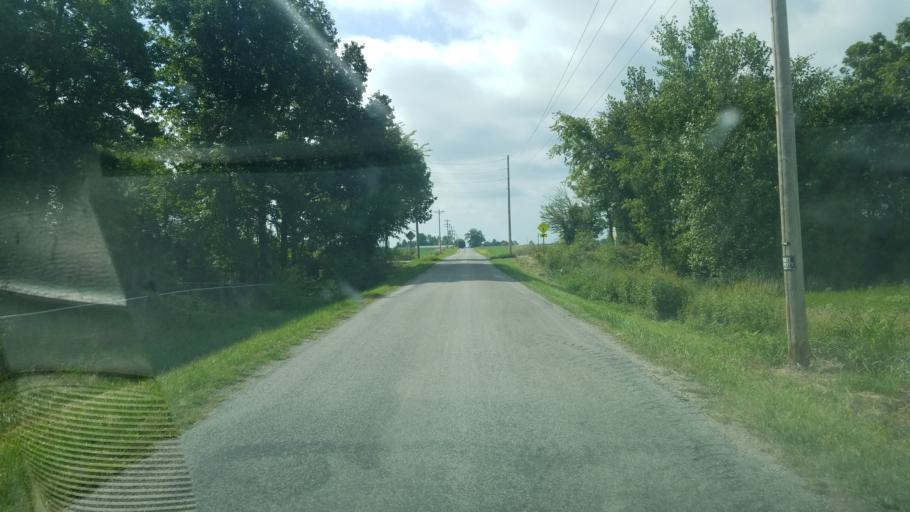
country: US
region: Ohio
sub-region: Union County
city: Richwood
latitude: 40.6070
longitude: -83.3617
